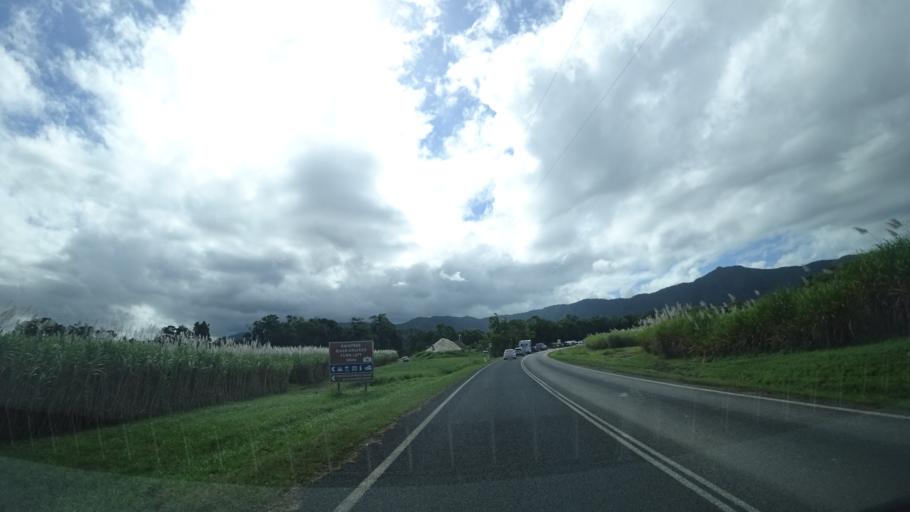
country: AU
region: Queensland
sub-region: Cairns
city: Port Douglas
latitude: -16.2638
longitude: 145.3926
